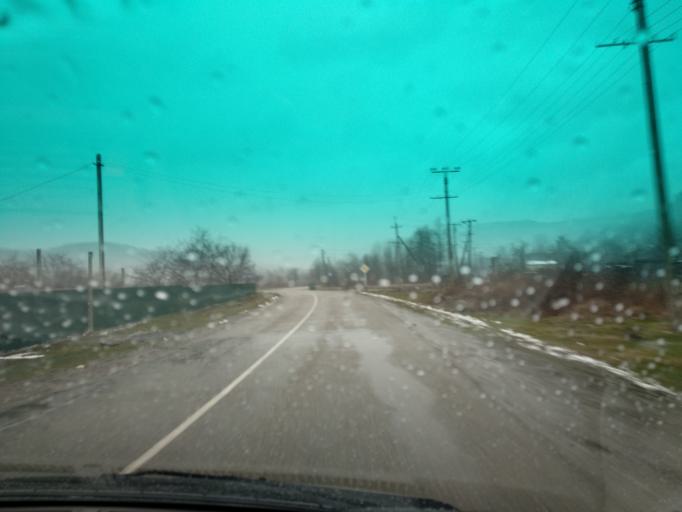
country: RU
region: Krasnodarskiy
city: Khadyzhensk
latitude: 44.2411
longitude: 39.3788
